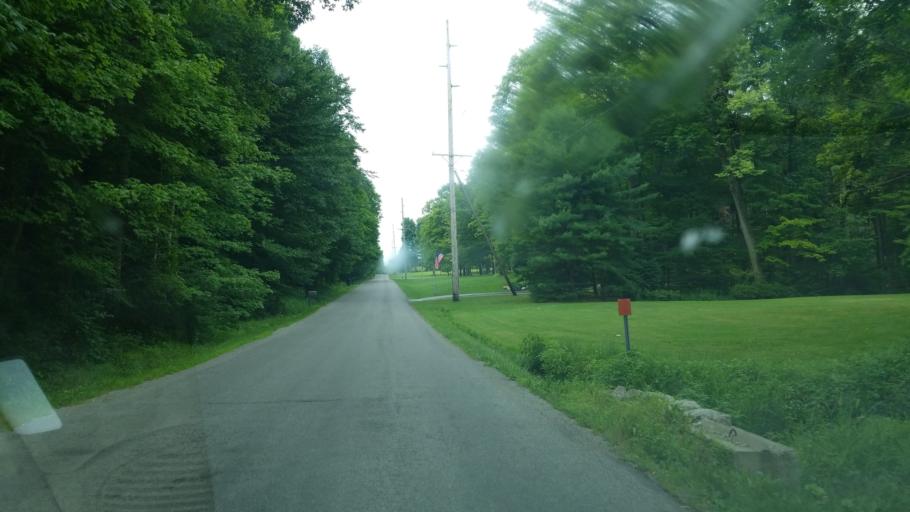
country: US
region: Ohio
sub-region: Ashland County
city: Ashland
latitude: 40.8507
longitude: -82.2889
